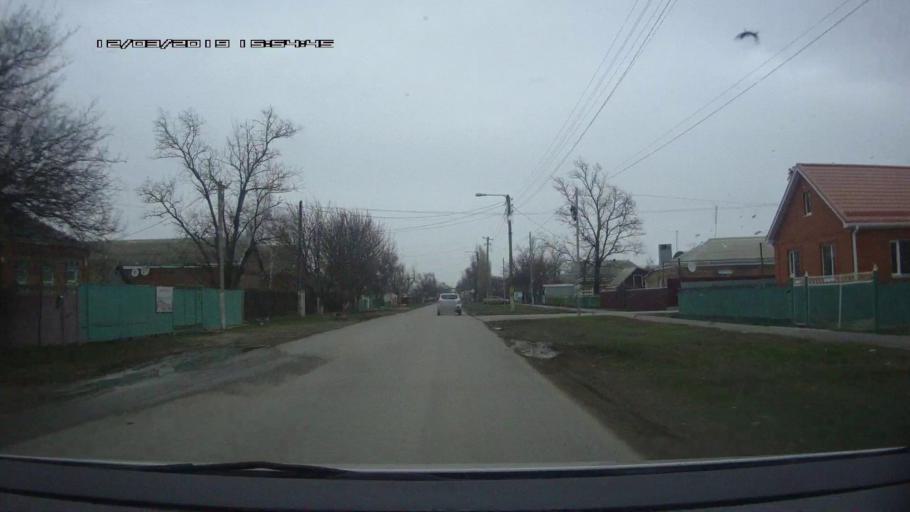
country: RU
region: Rostov
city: Novobataysk
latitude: 46.8925
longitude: 39.7783
